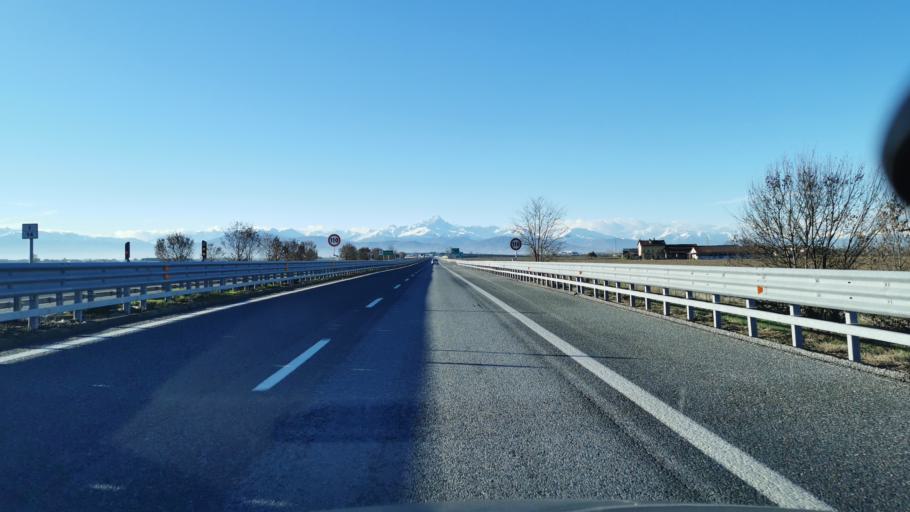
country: IT
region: Piedmont
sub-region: Provincia di Cuneo
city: Sant'Albano Stura
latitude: 44.4721
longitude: 7.7074
